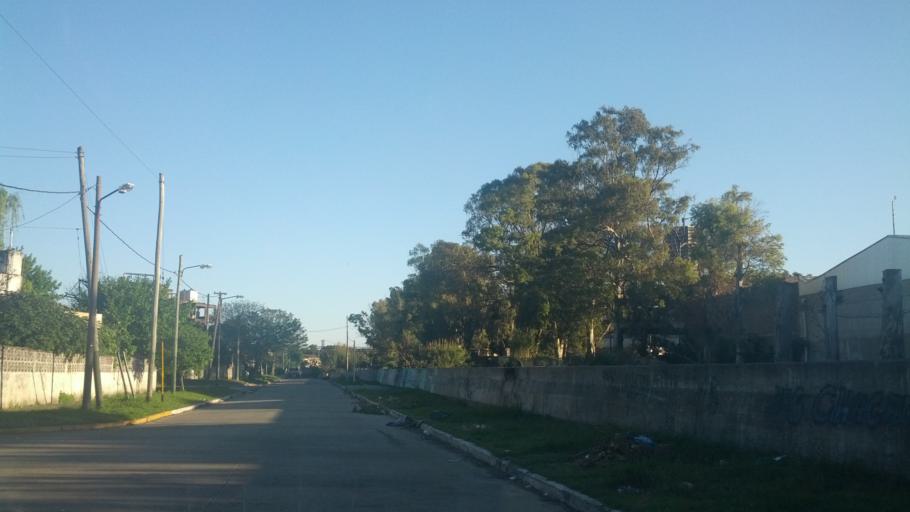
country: AR
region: Buenos Aires
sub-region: Partido de Lomas de Zamora
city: Lomas de Zamora
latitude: -34.7614
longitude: -58.4295
